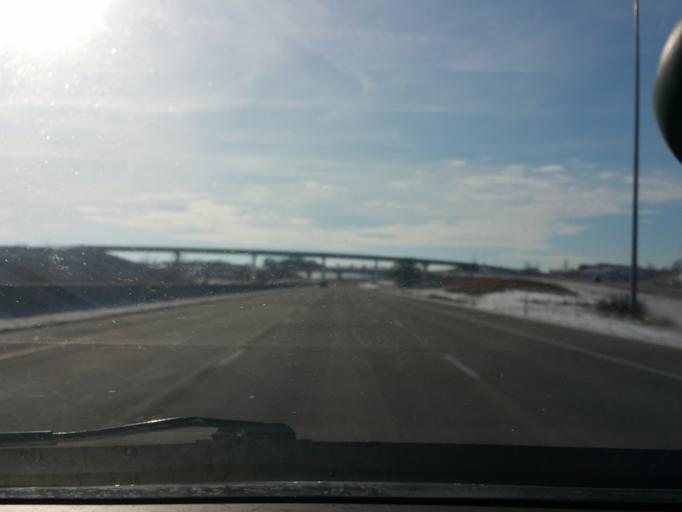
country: US
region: Iowa
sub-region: Polk County
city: West Des Moines
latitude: 41.5289
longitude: -93.7736
